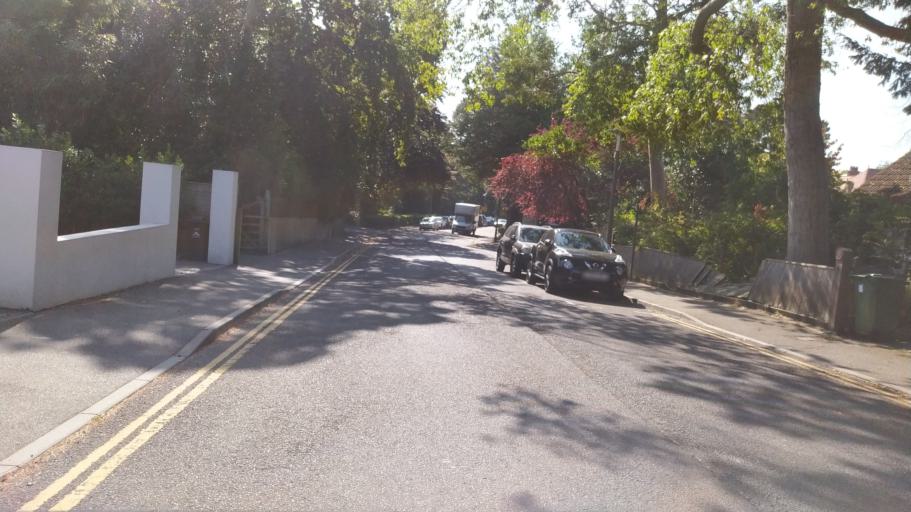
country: GB
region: England
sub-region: Dorset
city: Parkstone
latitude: 50.7042
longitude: -1.9222
